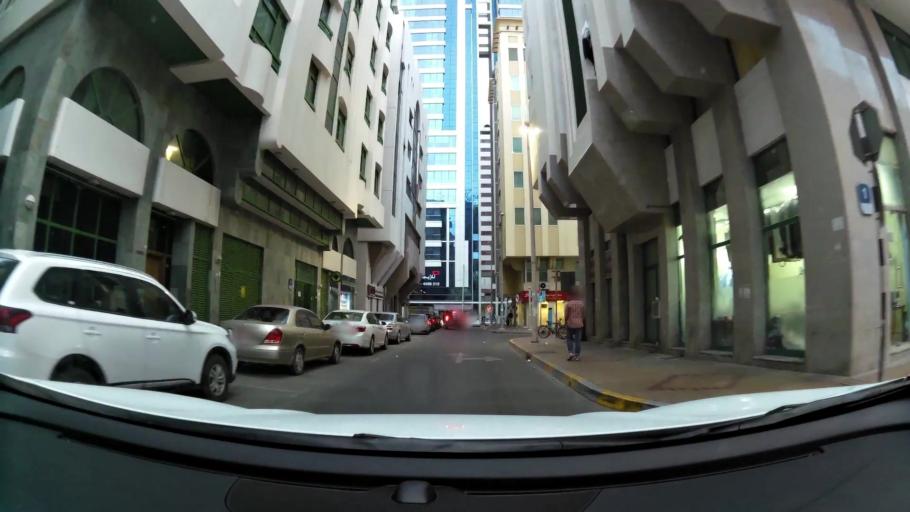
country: AE
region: Abu Dhabi
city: Abu Dhabi
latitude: 24.4897
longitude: 54.3722
